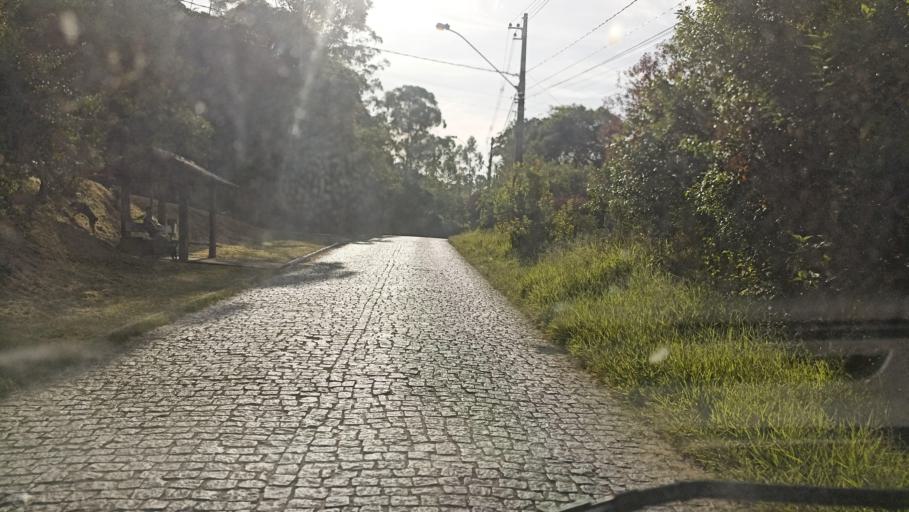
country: BR
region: Minas Gerais
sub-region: Tiradentes
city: Tiradentes
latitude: -21.1193
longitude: -44.1993
